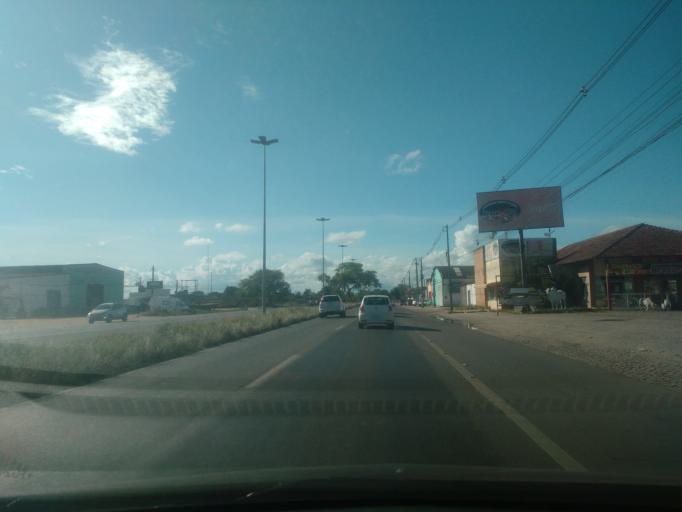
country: BR
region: Alagoas
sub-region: Satuba
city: Satuba
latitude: -9.5310
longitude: -35.7967
